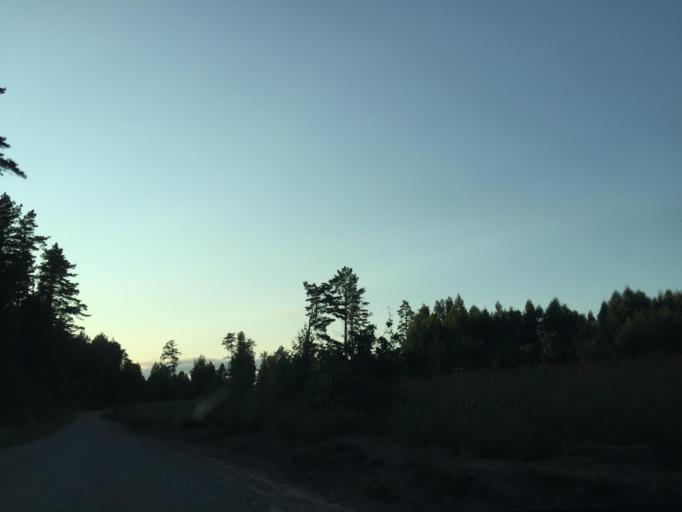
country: LV
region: Kuldigas Rajons
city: Kuldiga
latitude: 57.1180
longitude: 22.2129
